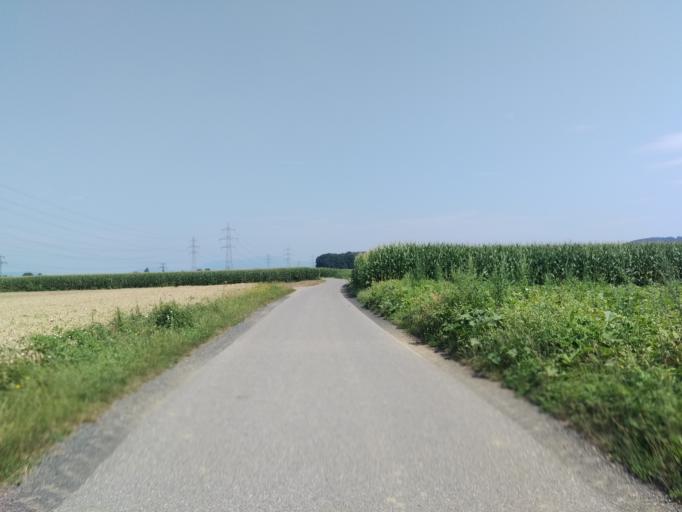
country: AT
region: Styria
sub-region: Politischer Bezirk Graz-Umgebung
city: Werndorf
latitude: 46.9296
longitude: 15.4899
